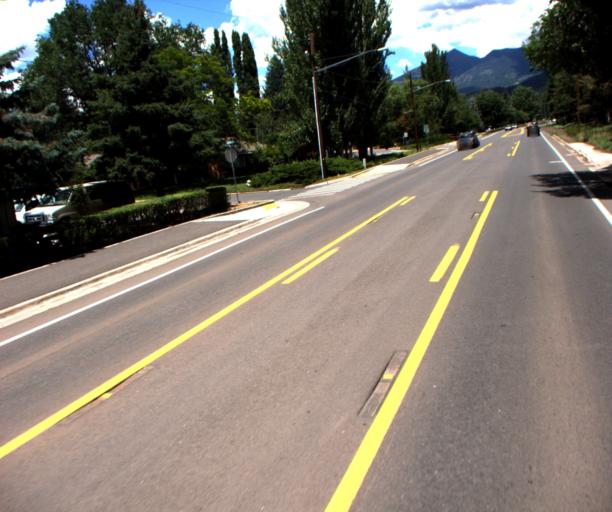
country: US
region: Arizona
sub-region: Coconino County
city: Flagstaff
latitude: 35.2134
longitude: -111.6502
